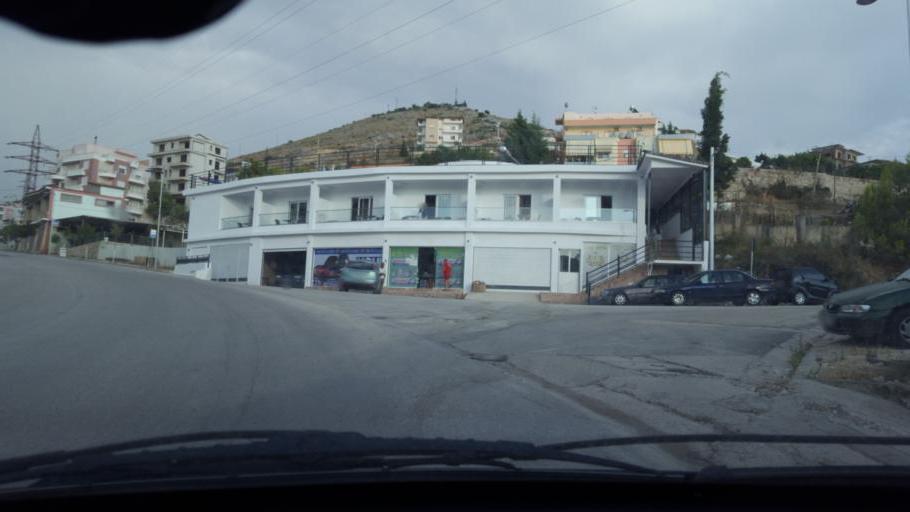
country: AL
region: Vlore
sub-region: Rrethi i Sarandes
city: Sarande
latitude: 39.8687
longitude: 20.0198
